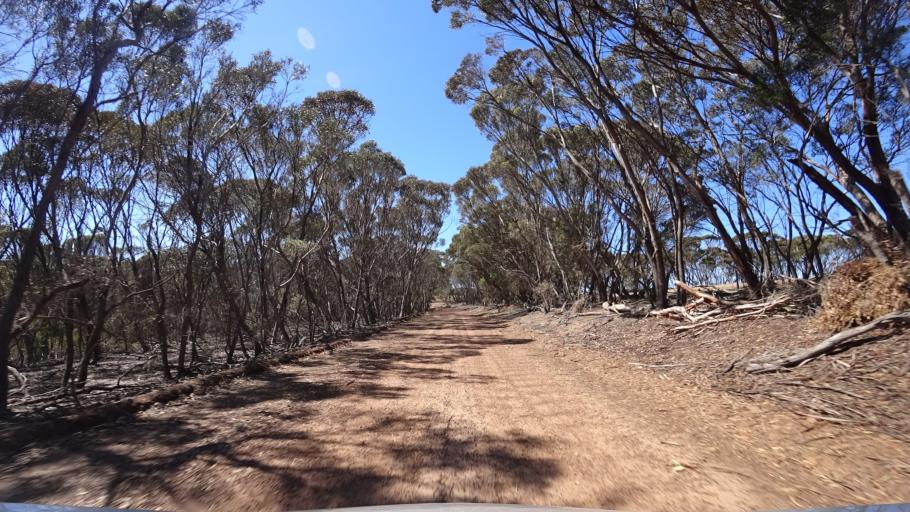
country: AU
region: South Australia
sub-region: Kangaroo Island
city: Kingscote
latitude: -35.7485
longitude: 137.7267
